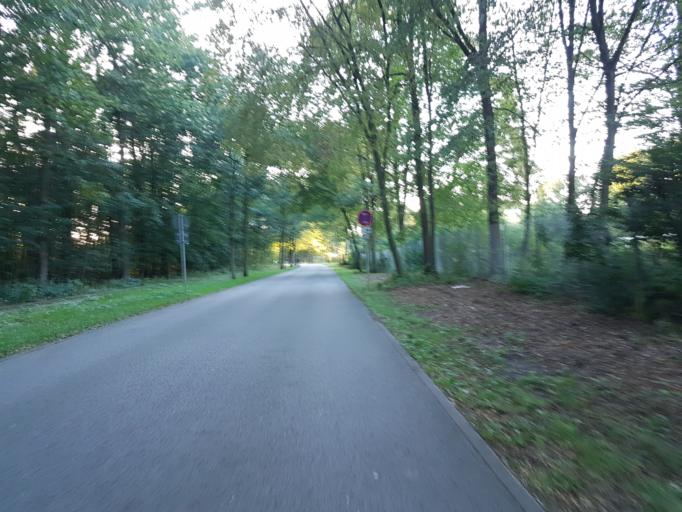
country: DE
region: Lower Saxony
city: Langenhagen
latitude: 52.4445
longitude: 9.7600
